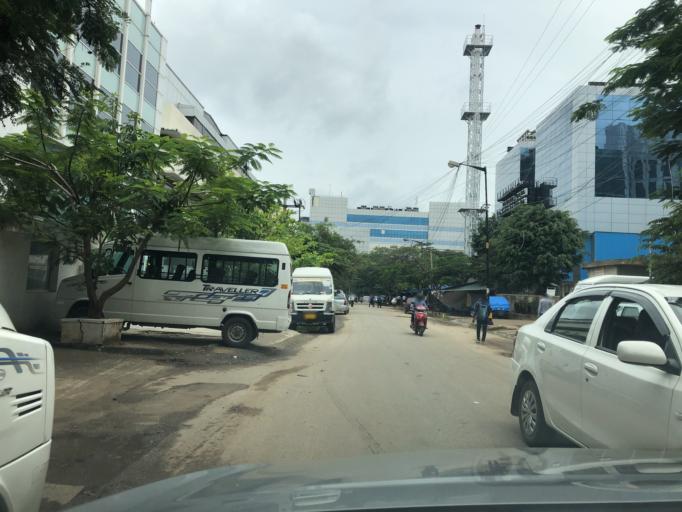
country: IN
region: Karnataka
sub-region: Bangalore Rural
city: Hoskote
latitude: 12.9789
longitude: 77.7248
